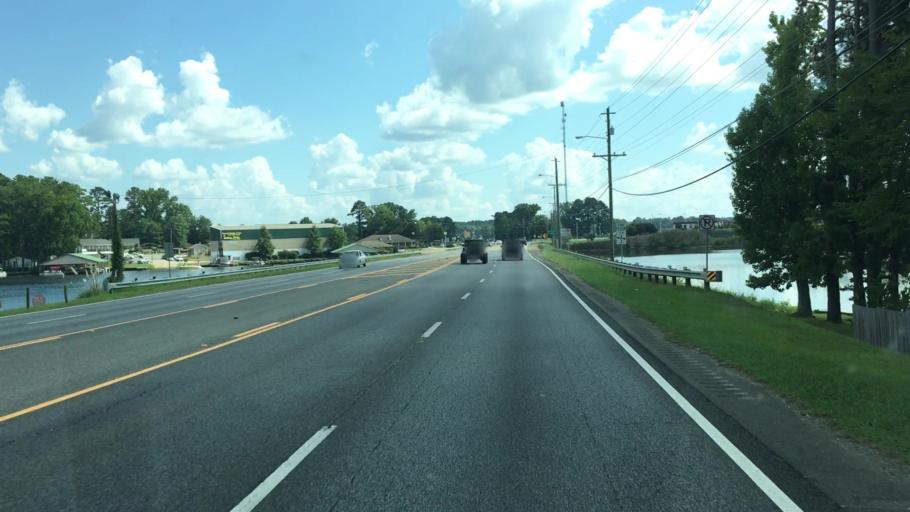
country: US
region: Georgia
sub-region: Baldwin County
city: Milledgeville
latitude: 33.1983
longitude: -83.2952
